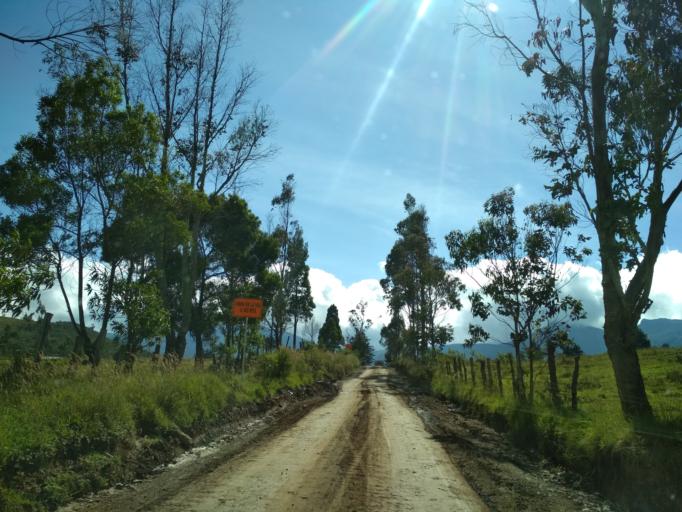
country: CO
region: Cauca
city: Silvia
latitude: 2.6931
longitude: -76.3347
